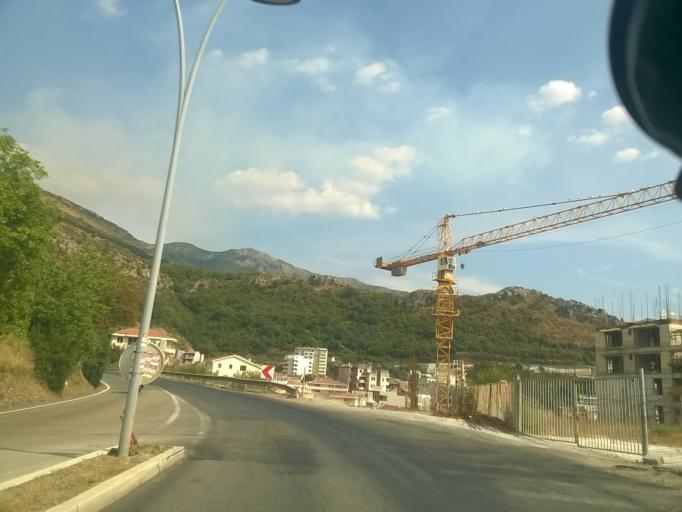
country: ME
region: Budva
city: Budva
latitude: 42.2815
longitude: 18.8787
